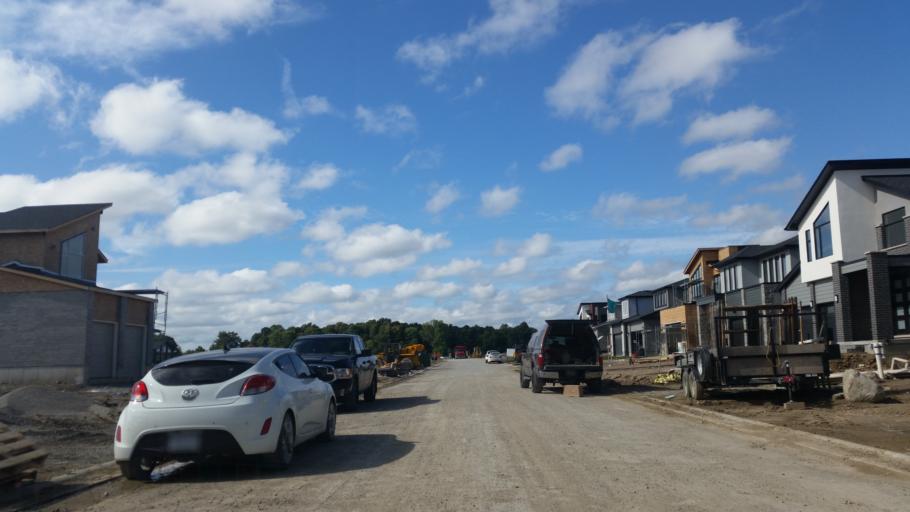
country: CA
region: Ontario
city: London
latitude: 43.0207
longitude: -81.3337
